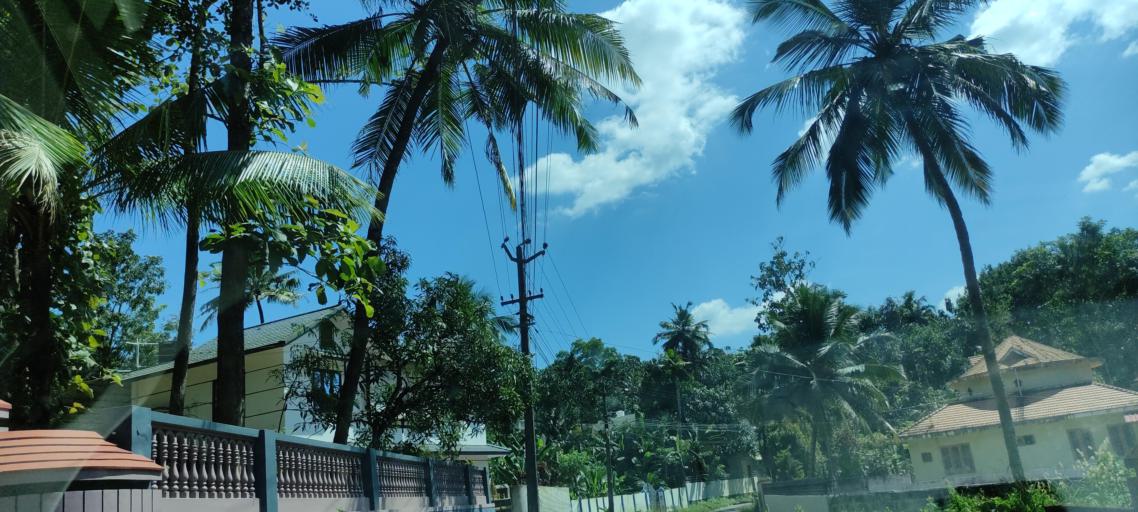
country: IN
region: Kerala
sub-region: Pattanamtitta
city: Adur
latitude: 9.1059
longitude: 76.6881
